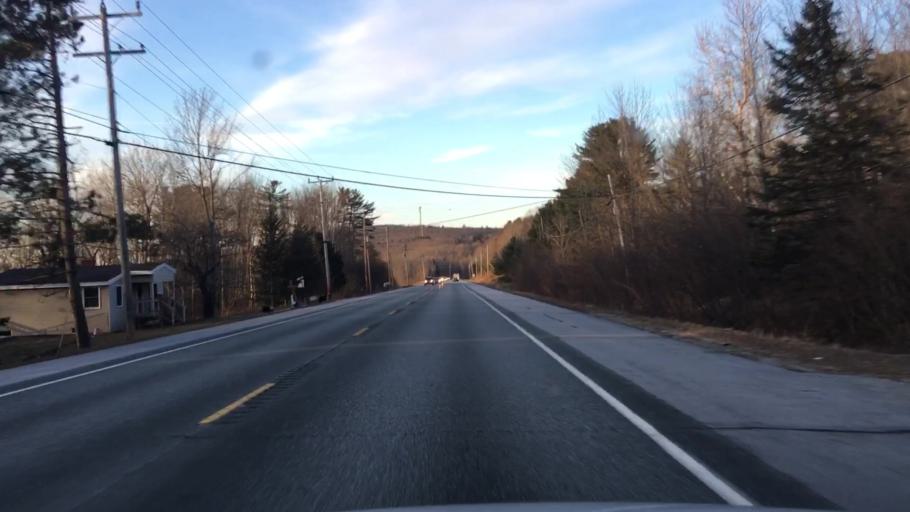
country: US
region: Maine
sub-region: Hancock County
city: Dedham
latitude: 44.7090
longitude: -68.6019
